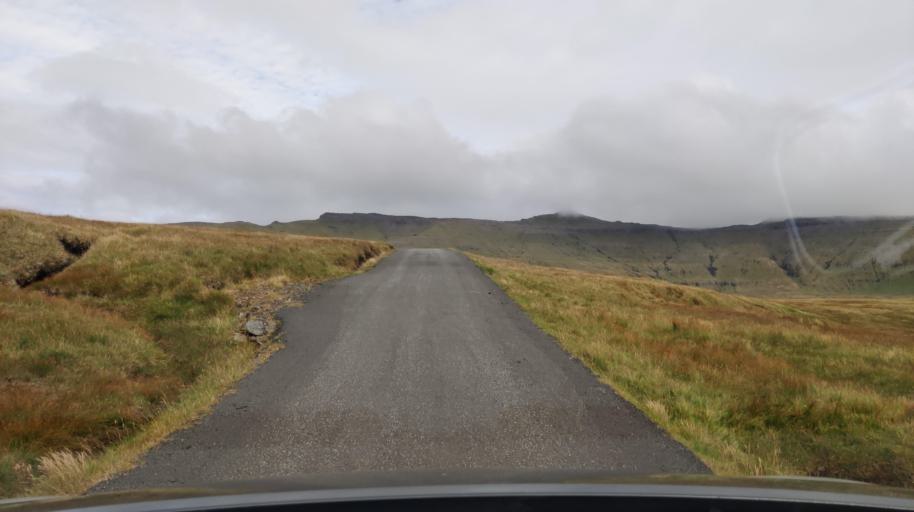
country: FO
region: Streymoy
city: Vestmanna
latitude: 62.1609
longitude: -7.1014
